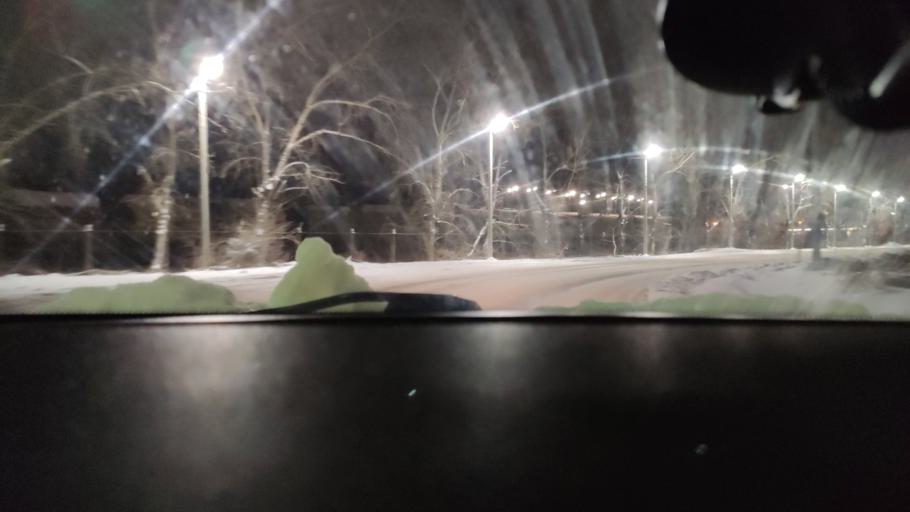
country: RU
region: Perm
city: Krasnokamsk
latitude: 58.0726
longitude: 55.7783
